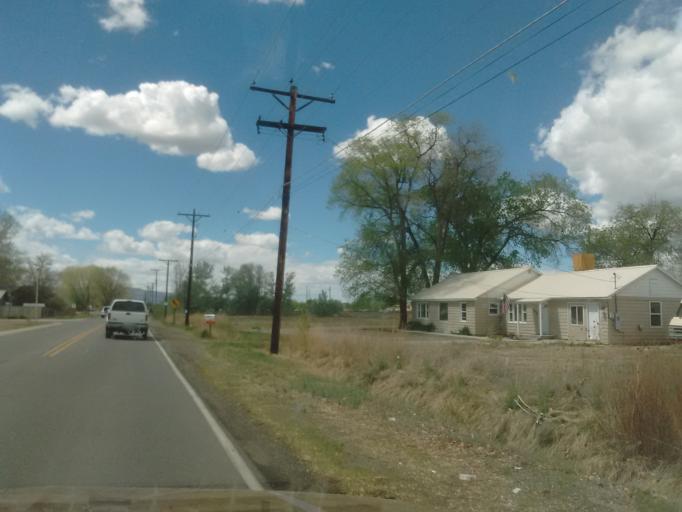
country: US
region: Colorado
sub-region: Mesa County
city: Fruitvale
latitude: 39.0774
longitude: -108.4900
